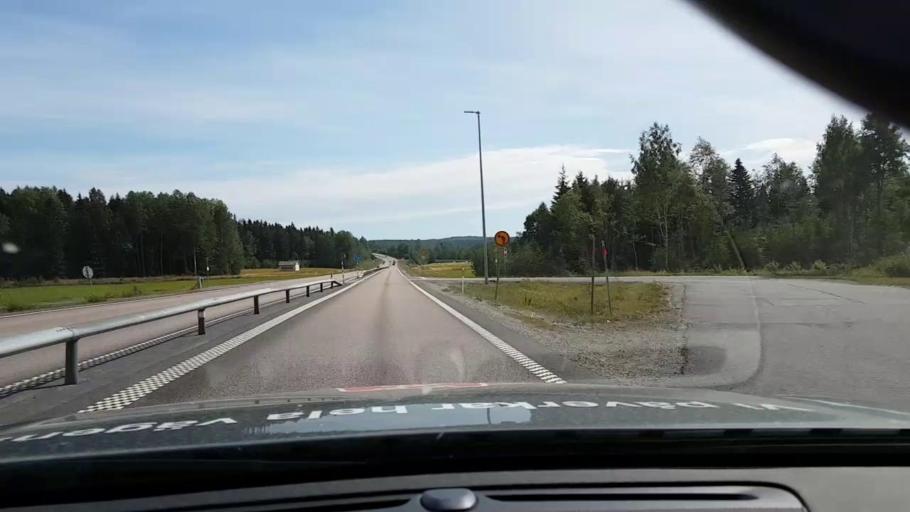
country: SE
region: Vaesternorrland
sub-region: OErnskoeldsviks Kommun
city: Ornskoldsvik
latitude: 63.3025
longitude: 18.8589
